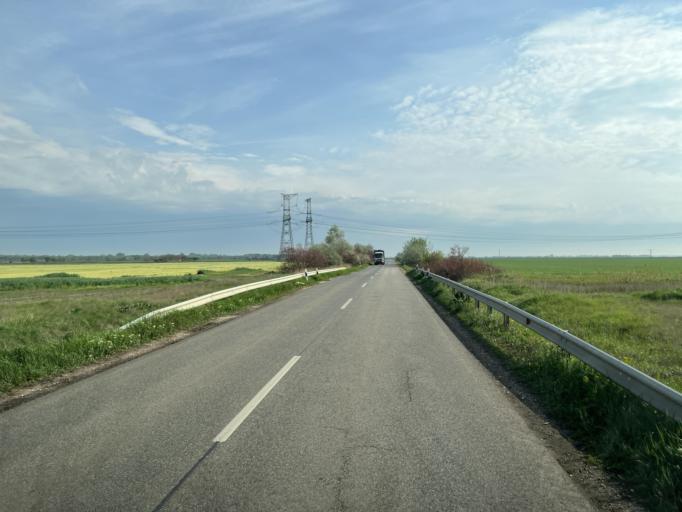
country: HU
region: Pest
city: Cegled
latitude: 47.2331
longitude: 19.7750
